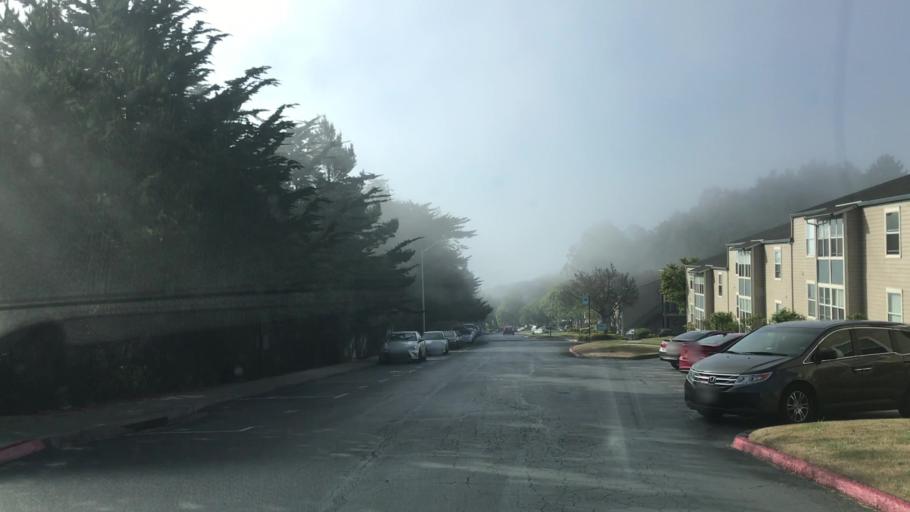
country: US
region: California
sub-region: San Mateo County
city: Broadmoor
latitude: 37.6654
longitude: -122.4794
